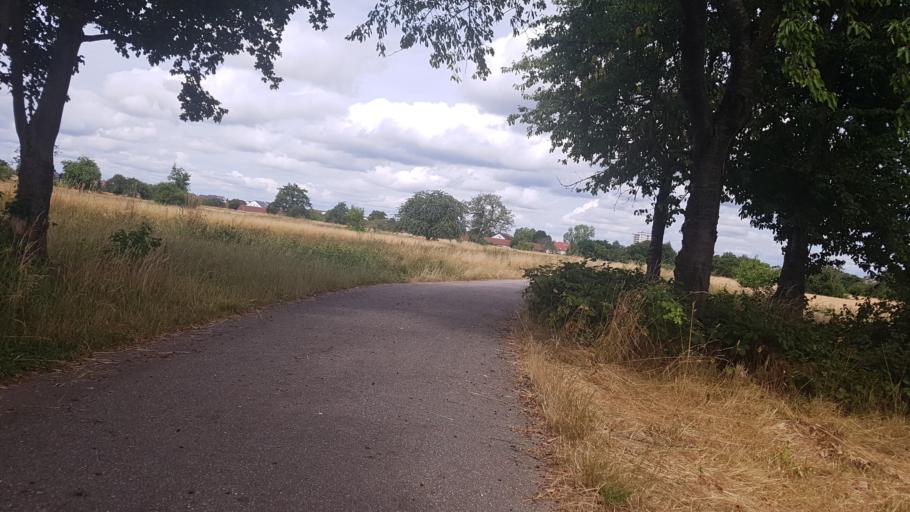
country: DE
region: Baden-Wuerttemberg
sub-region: Karlsruhe Region
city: Rheinstetten
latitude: 48.9741
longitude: 8.3256
